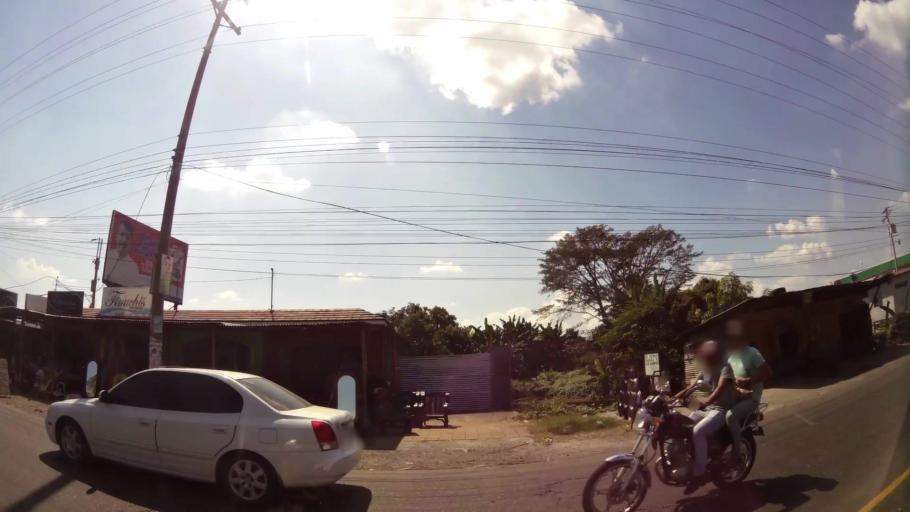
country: GT
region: Suchitepeque
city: Mazatenango
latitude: 14.5359
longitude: -91.4978
